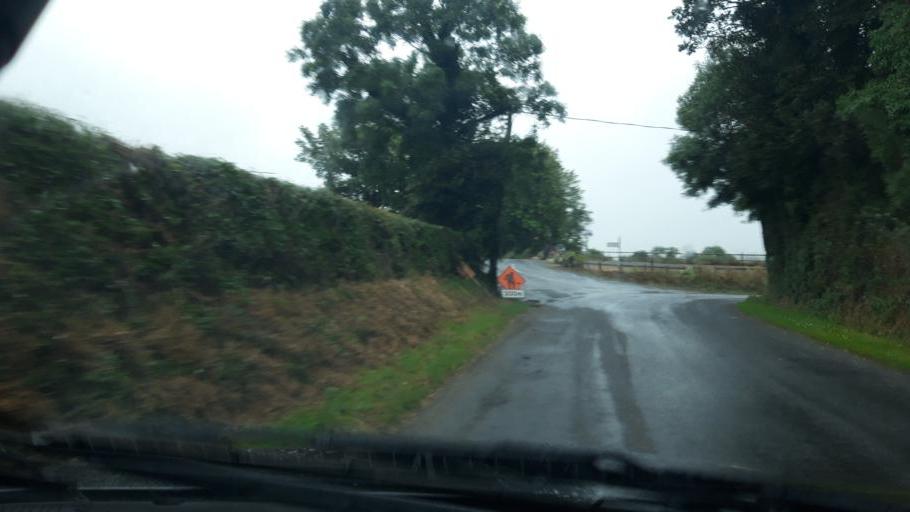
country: IE
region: Leinster
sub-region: Kilkenny
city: Callan
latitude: 52.6589
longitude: -7.4345
